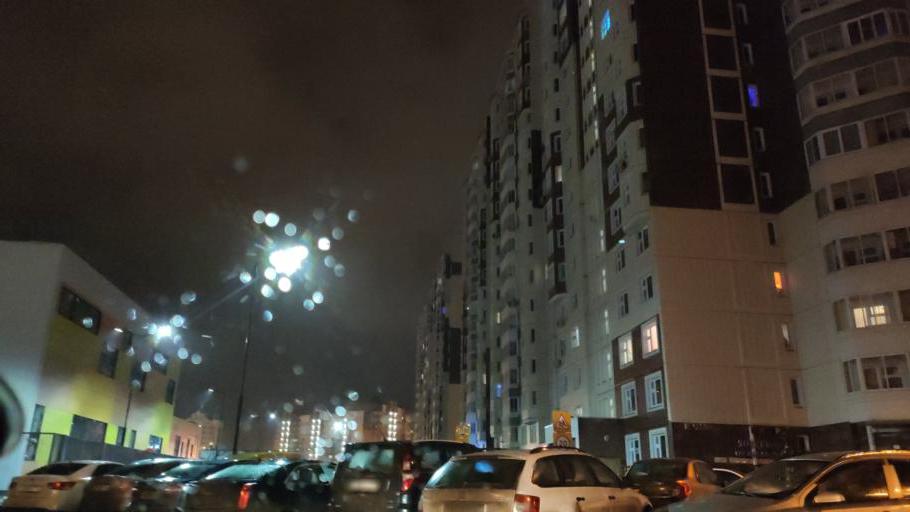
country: RU
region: Moskovskaya
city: Vatutinki
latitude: 55.5184
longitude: 37.3523
